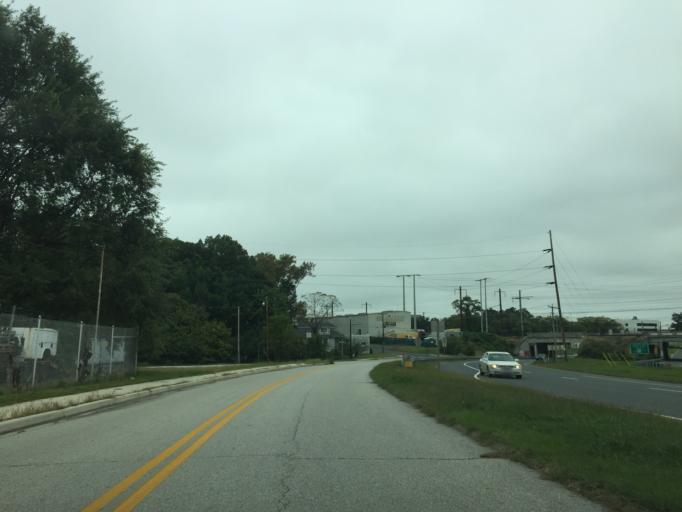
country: US
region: Maryland
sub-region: Baltimore County
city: Middle River
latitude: 39.3336
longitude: -76.4407
